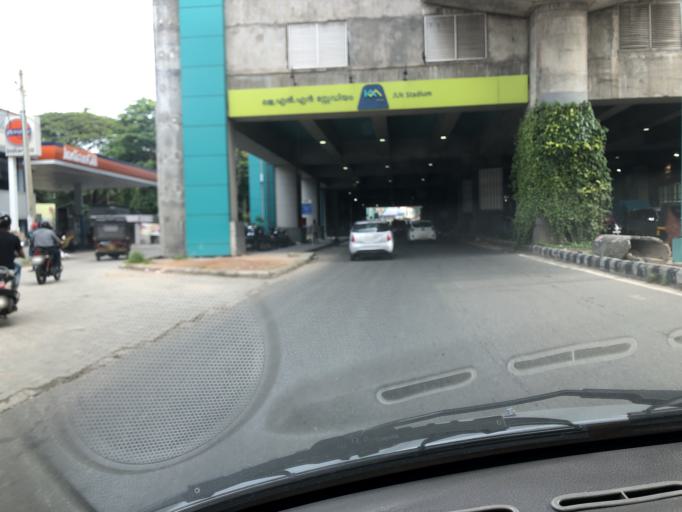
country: IN
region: Kerala
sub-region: Ernakulam
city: Elur
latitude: 9.9997
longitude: 76.2982
